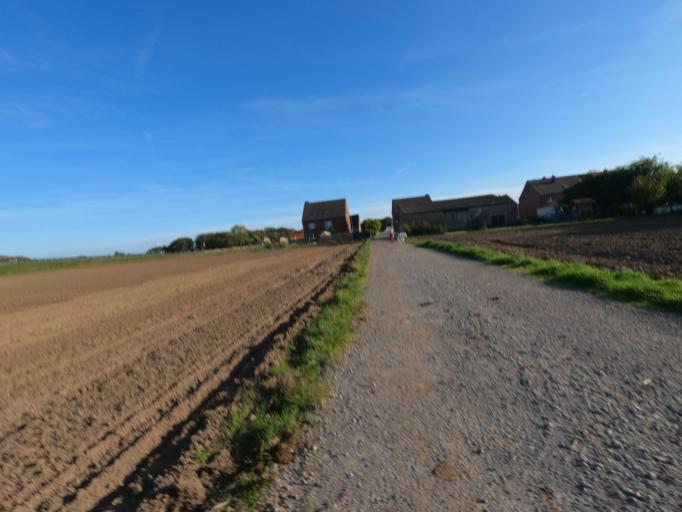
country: DE
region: North Rhine-Westphalia
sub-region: Regierungsbezirk Koln
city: Wassenberg
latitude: 51.1041
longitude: 6.2042
